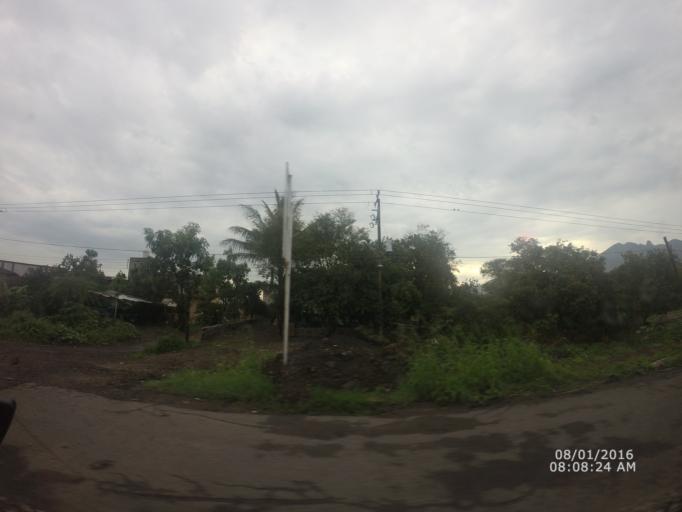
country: MX
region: Nayarit
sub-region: Tepic
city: La Corregidora
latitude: 21.4536
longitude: -104.8198
